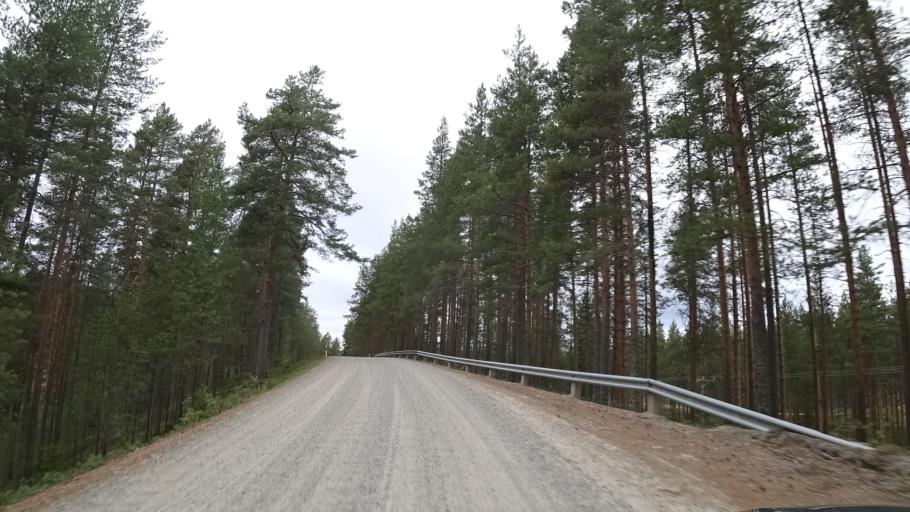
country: FI
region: North Karelia
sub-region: Pielisen Karjala
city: Lieksa
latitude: 63.2370
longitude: 30.3599
